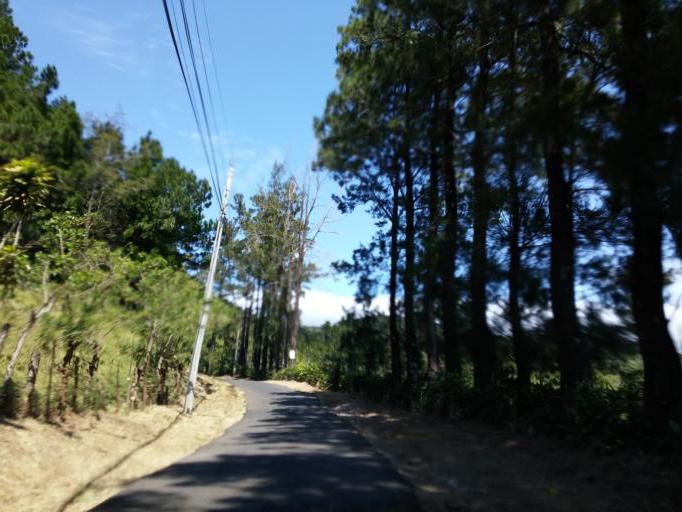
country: CR
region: Heredia
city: Santo Domingo
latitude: 10.0674
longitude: -84.1265
